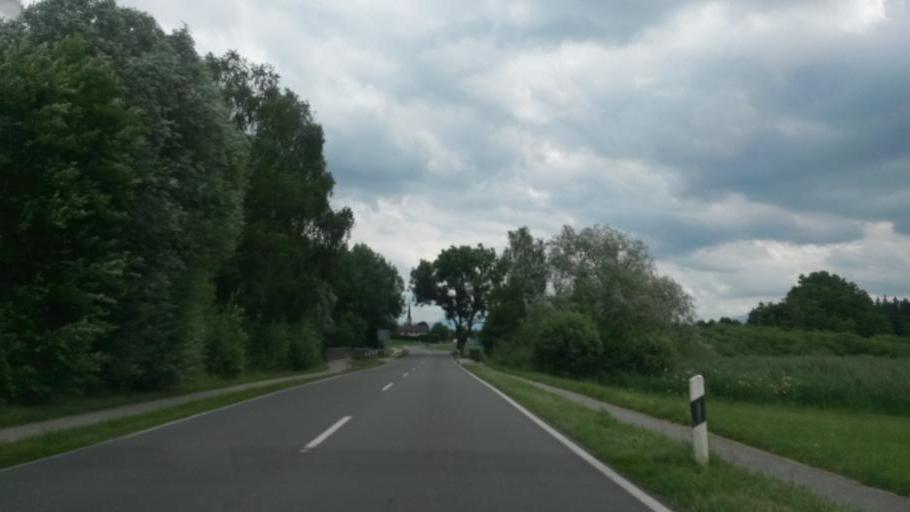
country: DE
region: Bavaria
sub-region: Upper Bavaria
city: Eggstatt
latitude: 47.9348
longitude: 12.3724
